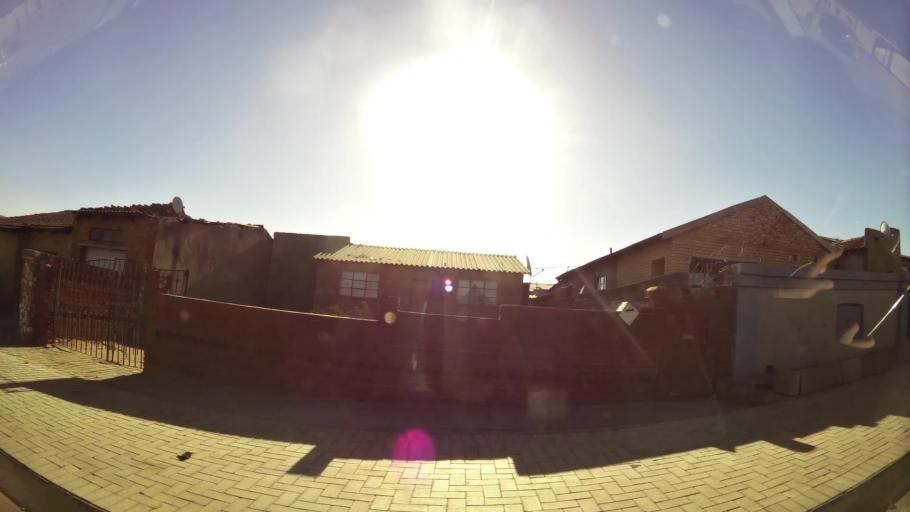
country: ZA
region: Gauteng
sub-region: Ekurhuleni Metropolitan Municipality
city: Tembisa
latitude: -26.0268
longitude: 28.2179
